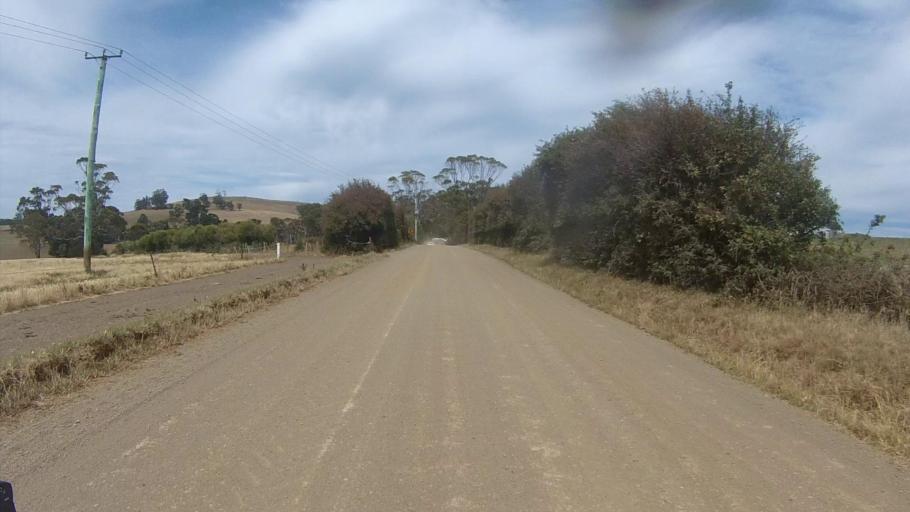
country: AU
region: Tasmania
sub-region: Sorell
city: Sorell
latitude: -42.8173
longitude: 147.8248
